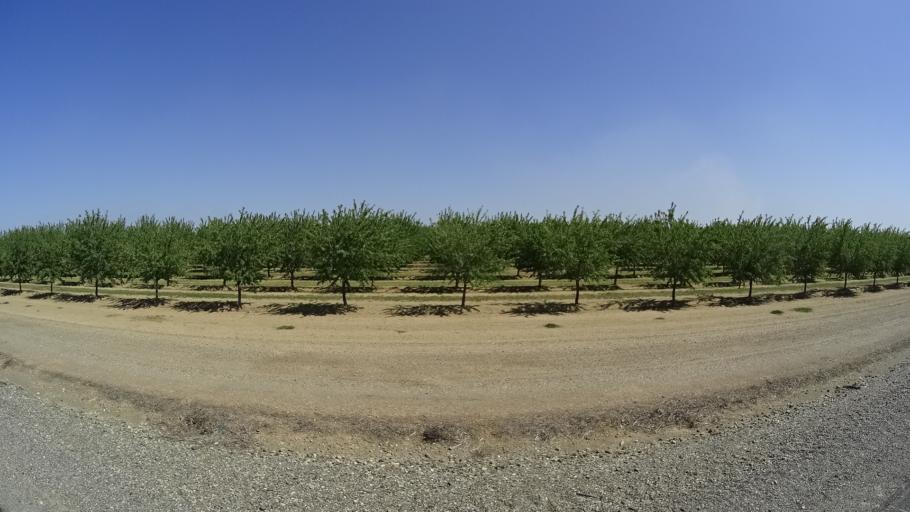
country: US
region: California
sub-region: Glenn County
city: Willows
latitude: 39.5730
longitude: -122.1370
